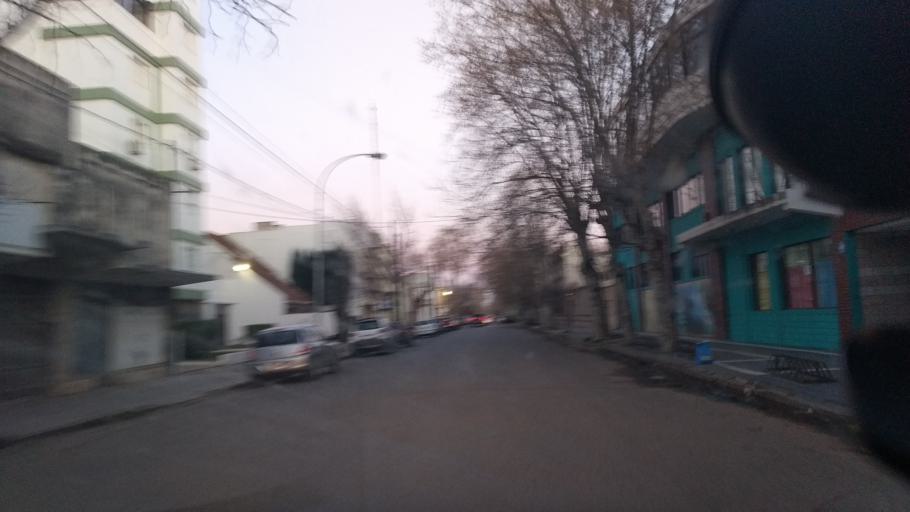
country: AR
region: Buenos Aires
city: Necochea
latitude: -38.5514
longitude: -58.7392
